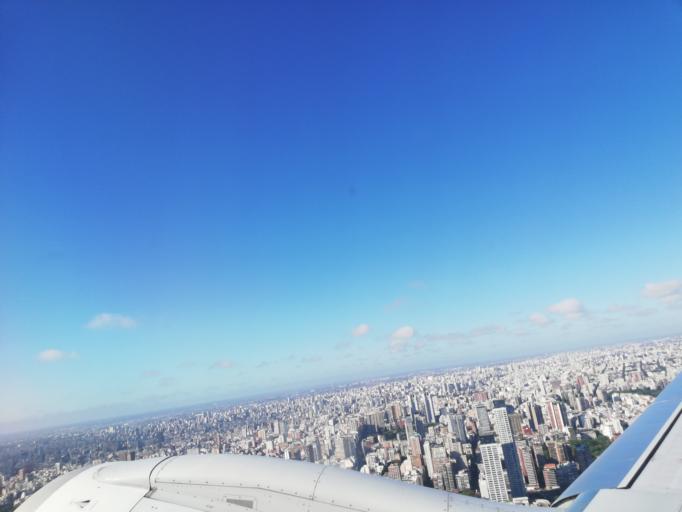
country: AR
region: Buenos Aires F.D.
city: Retiro
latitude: -34.5686
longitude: -58.3984
